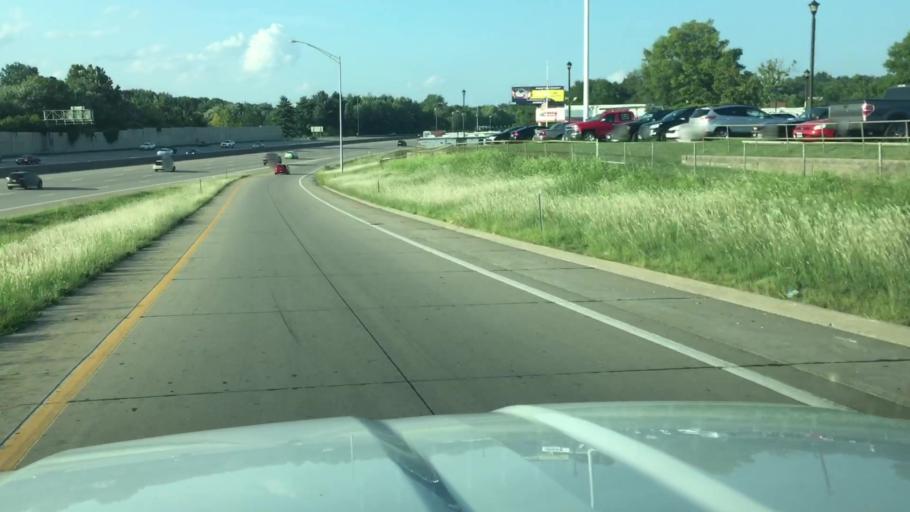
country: US
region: Missouri
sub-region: Jefferson County
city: Arnold
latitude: 38.4624
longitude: -90.3731
